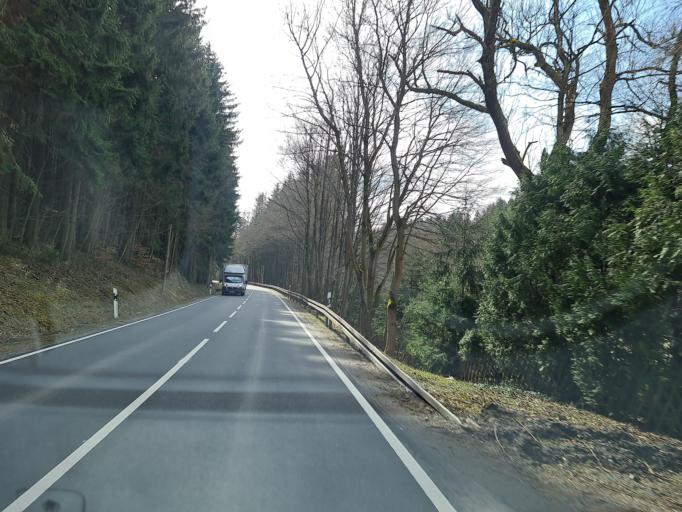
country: DE
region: Saxony
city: Wiesa
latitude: 50.6053
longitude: 12.9867
